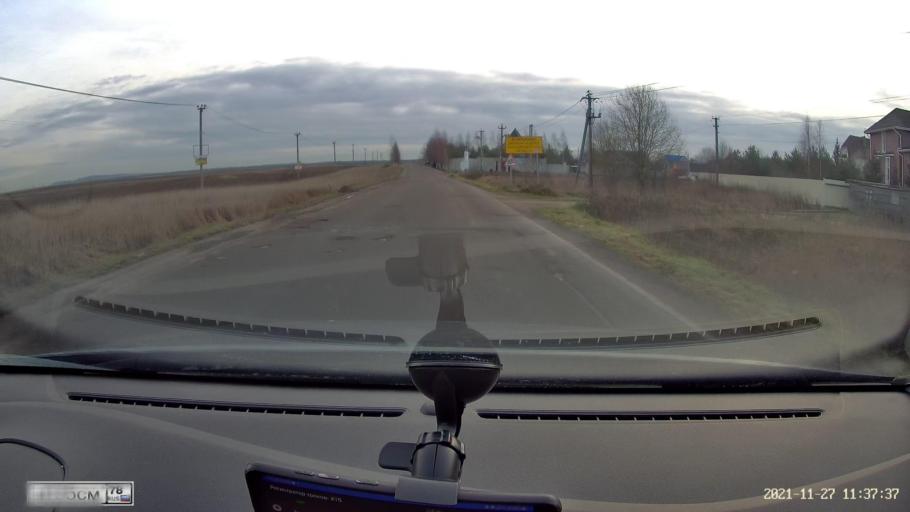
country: RU
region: Leningrad
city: Russko-Vysotskoye
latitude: 59.6929
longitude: 29.9892
